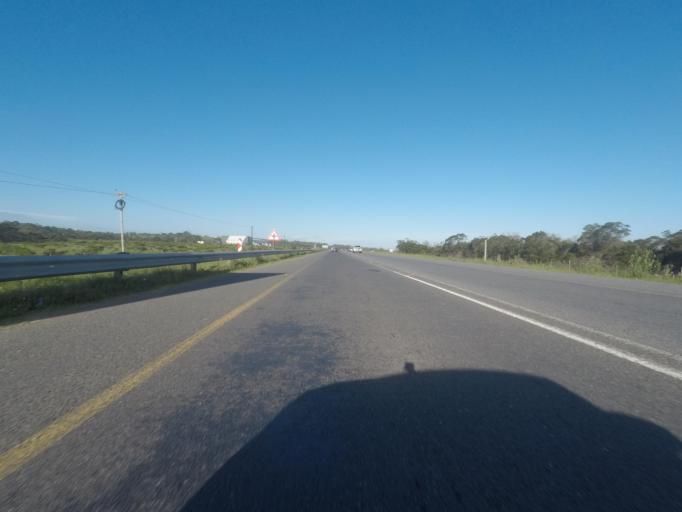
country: ZA
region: Eastern Cape
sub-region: Buffalo City Metropolitan Municipality
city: East London
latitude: -33.0537
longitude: 27.8060
